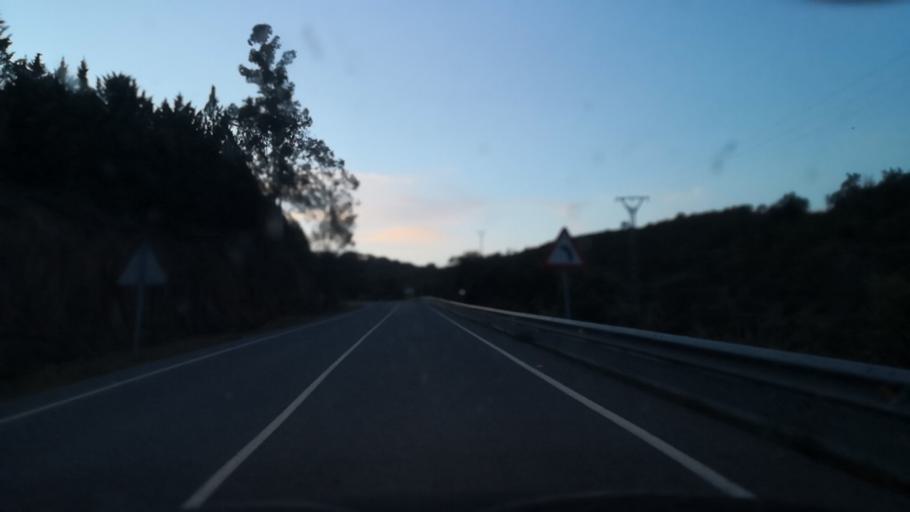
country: ES
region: Extremadura
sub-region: Provincia de Caceres
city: Alcantara
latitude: 39.7314
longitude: -6.8954
